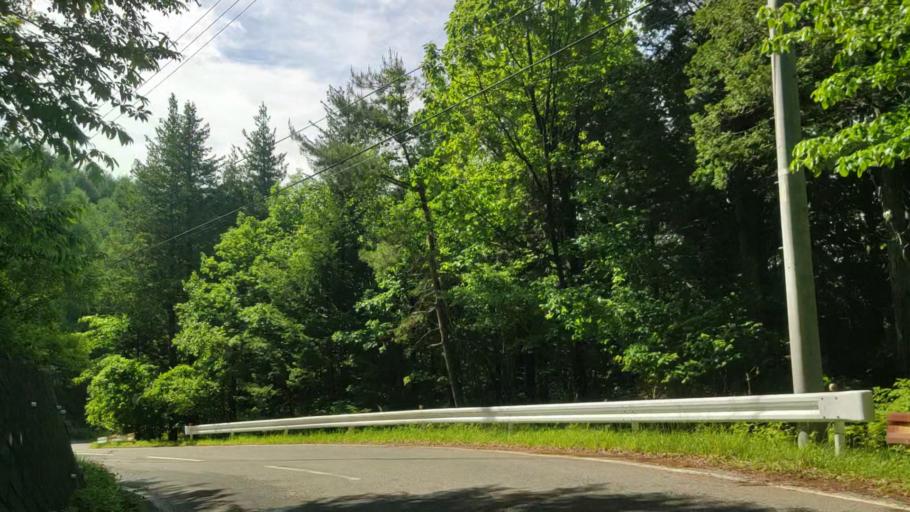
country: JP
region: Nagano
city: Suwa
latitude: 36.0929
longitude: 138.1447
